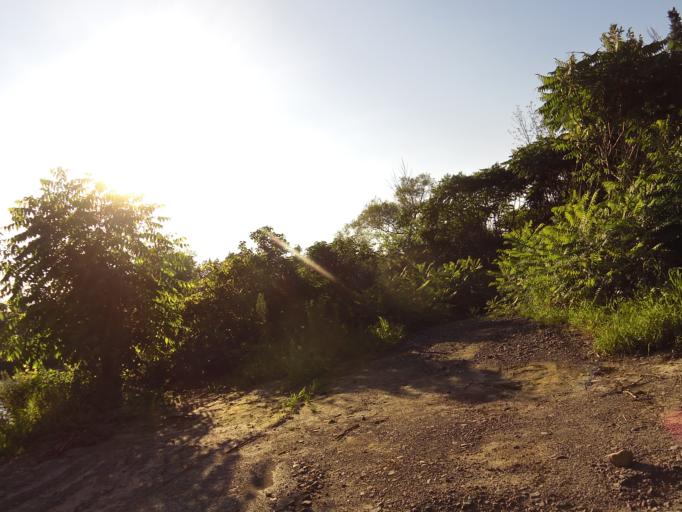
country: CA
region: Ontario
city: Ottawa
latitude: 45.3463
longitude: -75.6974
